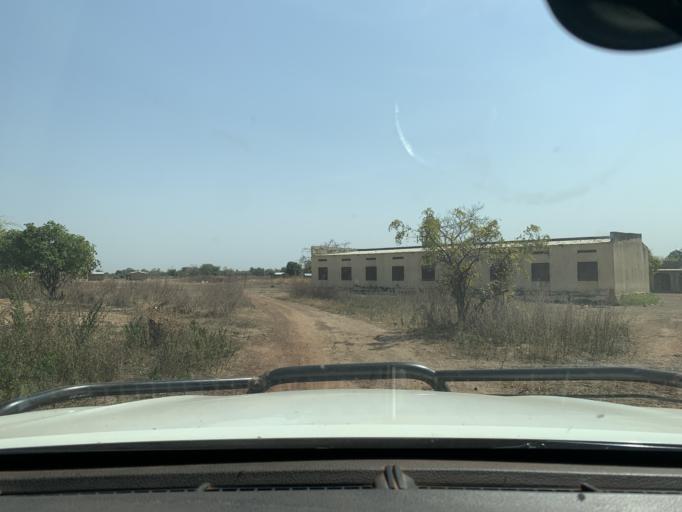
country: ML
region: Sikasso
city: Kolondieba
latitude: 10.8422
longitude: -6.8050
